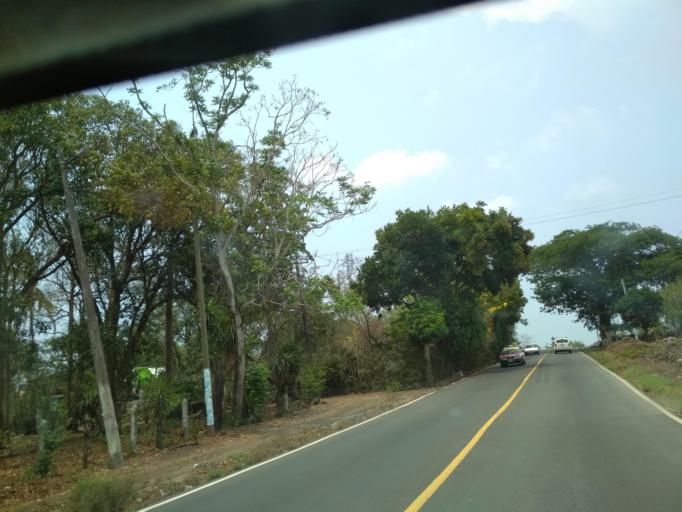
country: MX
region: Veracruz
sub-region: Veracruz
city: Delfino Victoria (Santa Fe)
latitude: 19.1730
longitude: -96.2757
